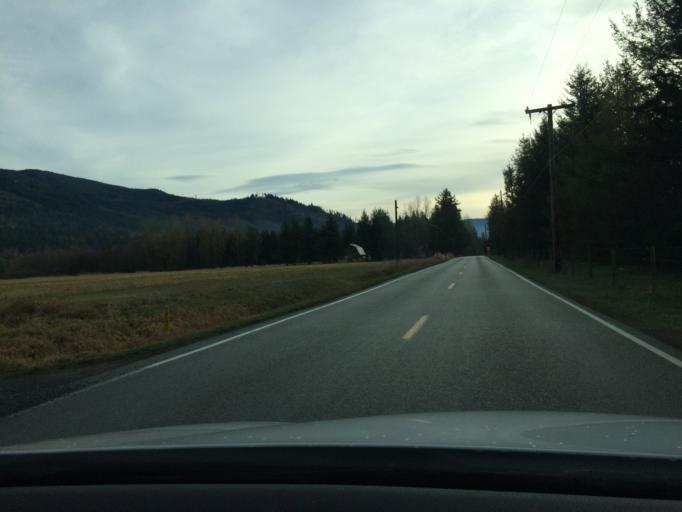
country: US
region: Washington
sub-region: Whatcom County
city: Nooksack
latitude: 48.9092
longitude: -122.2876
